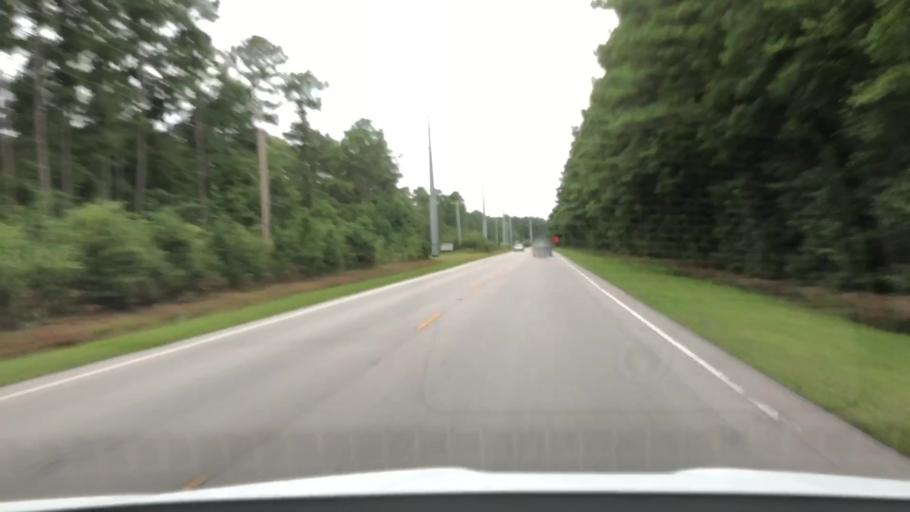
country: US
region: North Carolina
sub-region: Carteret County
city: Cape Carteret
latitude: 34.7438
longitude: -77.0883
